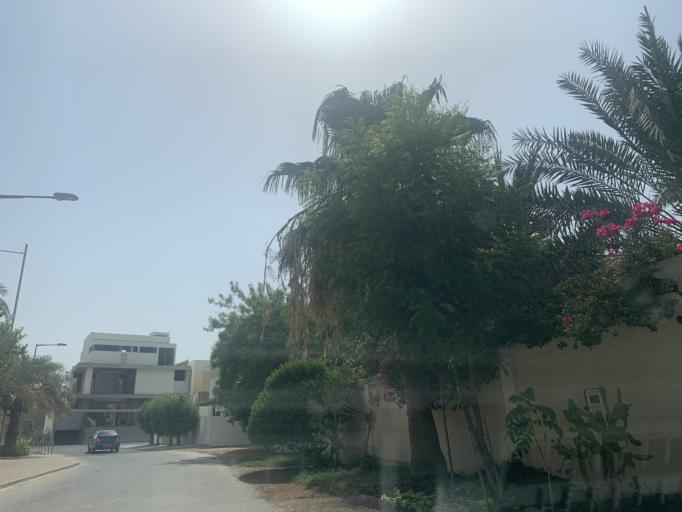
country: BH
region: Manama
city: Jidd Hafs
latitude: 26.1999
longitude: 50.5006
